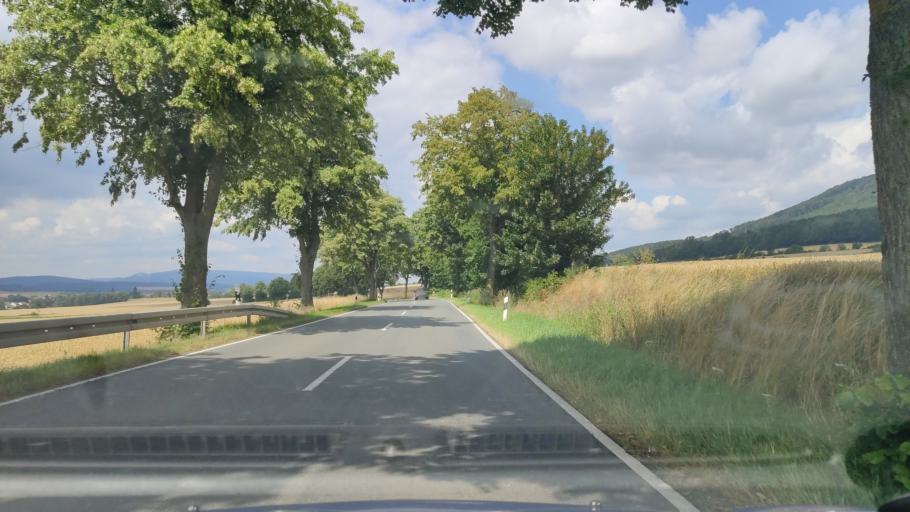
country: DE
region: Lower Saxony
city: Coppenbrugge
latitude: 52.0721
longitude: 9.5160
